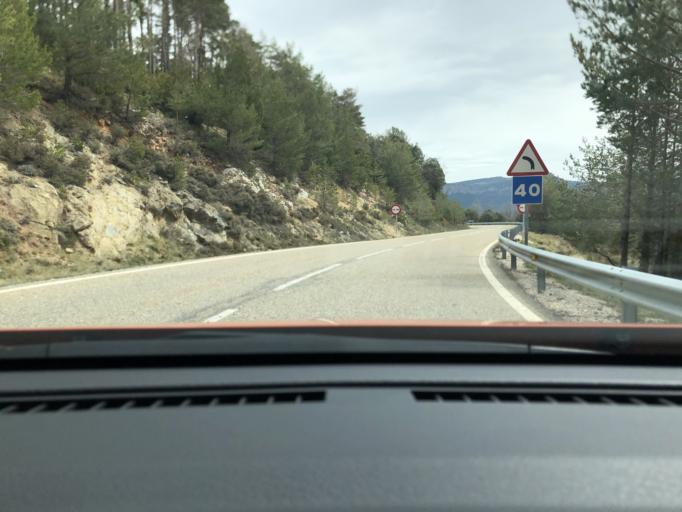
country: ES
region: Catalonia
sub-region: Provincia de Lleida
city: Olius
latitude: 42.1436
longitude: 1.5595
